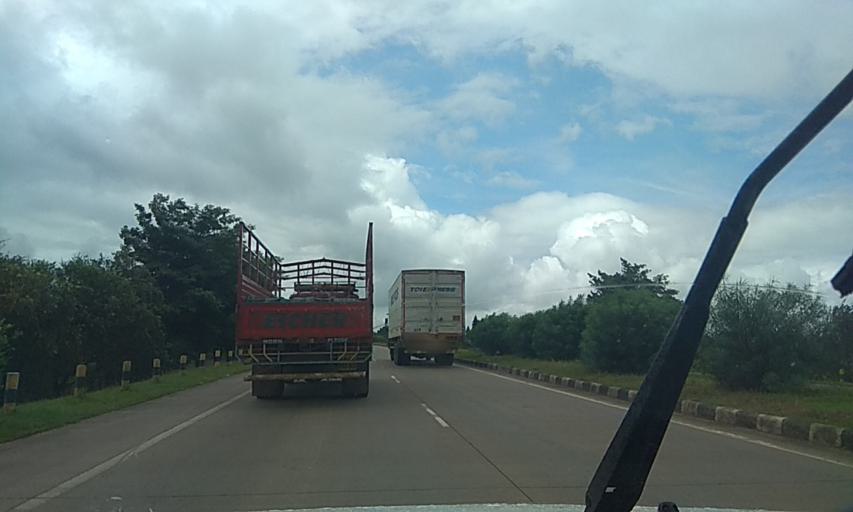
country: IN
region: Karnataka
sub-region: Belgaum
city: Sankeshwar
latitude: 16.3033
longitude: 74.4334
